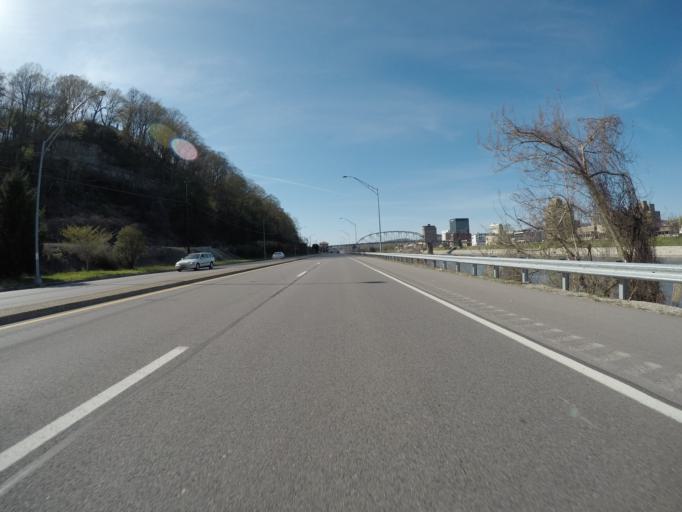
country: US
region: West Virginia
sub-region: Kanawha County
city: Charleston
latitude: 38.3429
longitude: -81.6343
